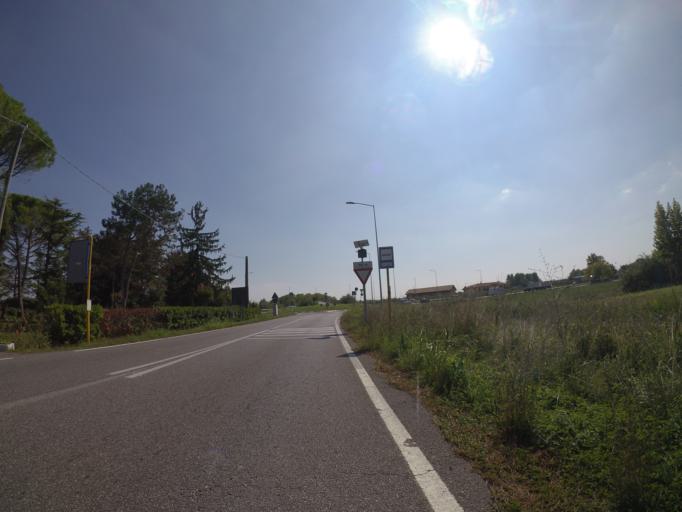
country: IT
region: Friuli Venezia Giulia
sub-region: Provincia di Udine
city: Palazzolo dello Stella
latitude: 45.8110
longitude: 13.1022
